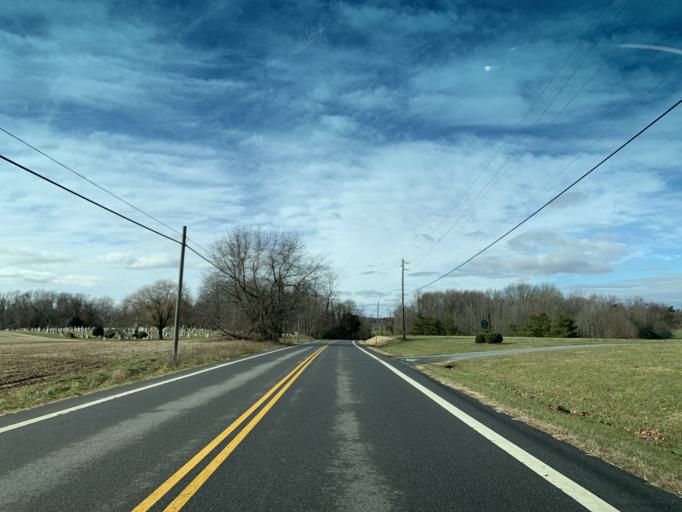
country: US
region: Maryland
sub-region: Kent County
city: Chestertown
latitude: 39.3283
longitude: -76.0515
